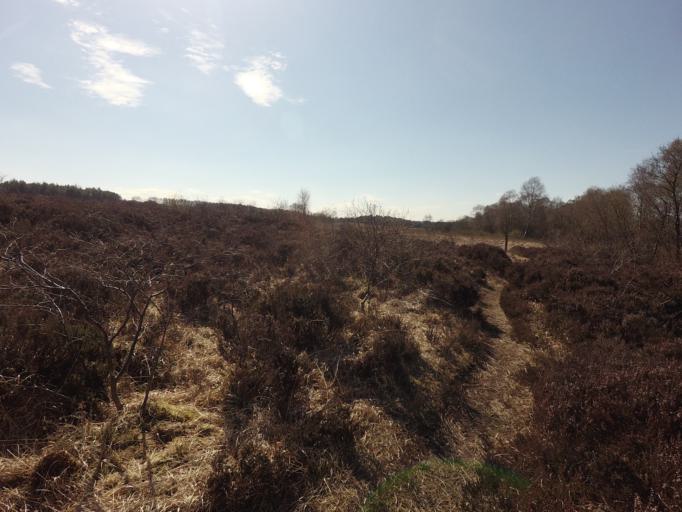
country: GB
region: Scotland
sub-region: West Lothian
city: West Calder
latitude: 55.8945
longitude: -3.5840
